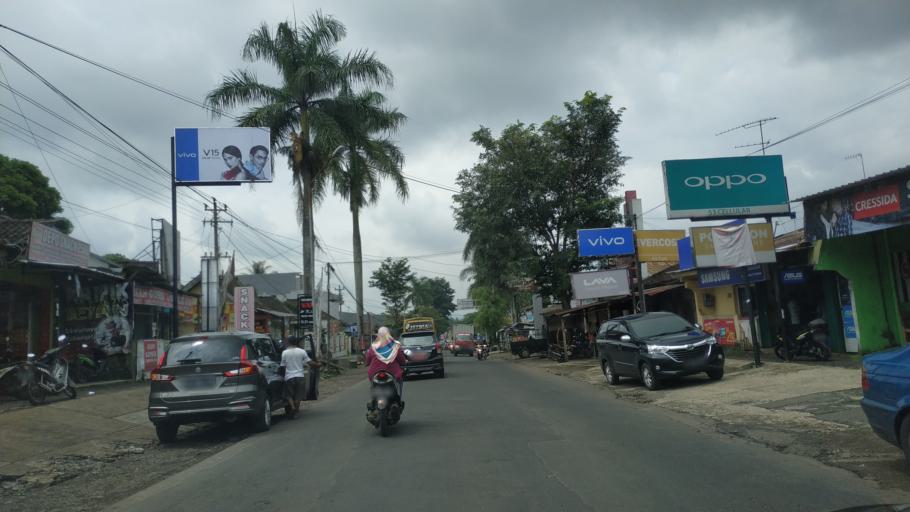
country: ID
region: Central Java
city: Weleri
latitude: -7.0881
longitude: 110.0466
